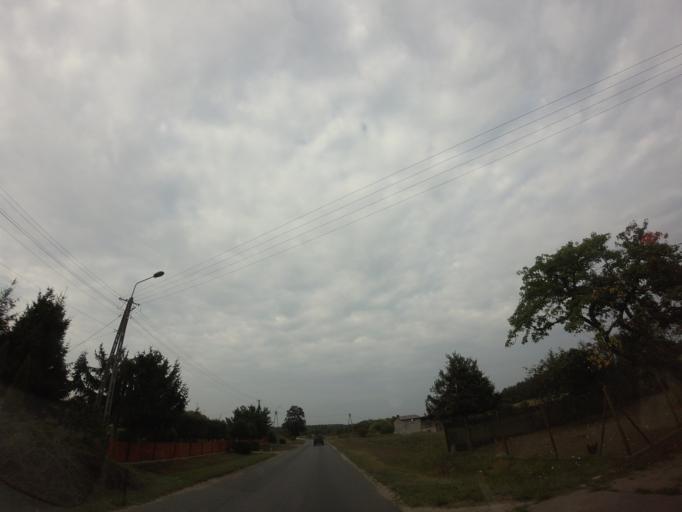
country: PL
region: West Pomeranian Voivodeship
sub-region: Powiat drawski
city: Drawsko Pomorskie
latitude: 53.4955
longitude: 15.7818
